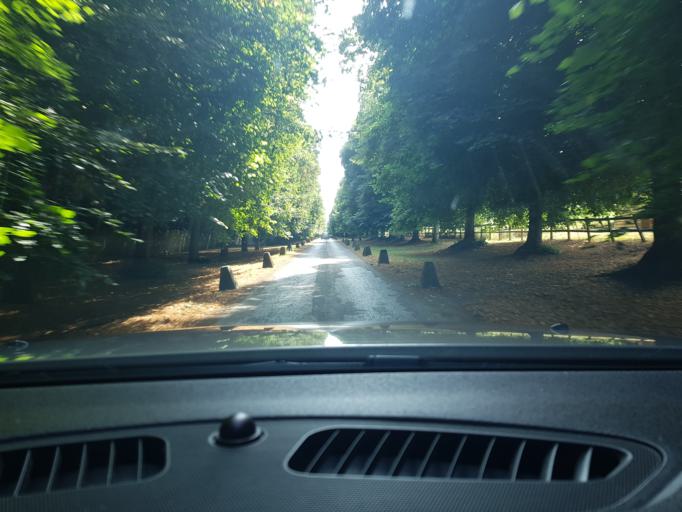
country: GB
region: England
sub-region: Wiltshire
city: Chilton Foliat
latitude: 51.4305
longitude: -1.5608
